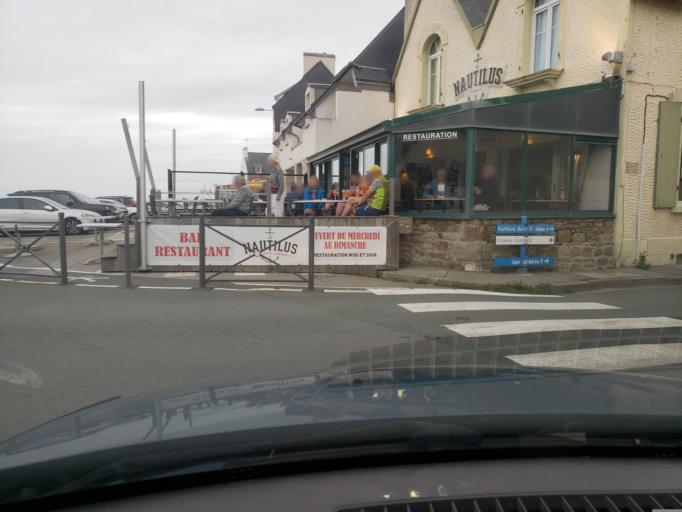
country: FR
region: Brittany
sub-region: Departement du Finistere
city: Guilvinec
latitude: 47.7973
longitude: -4.3551
